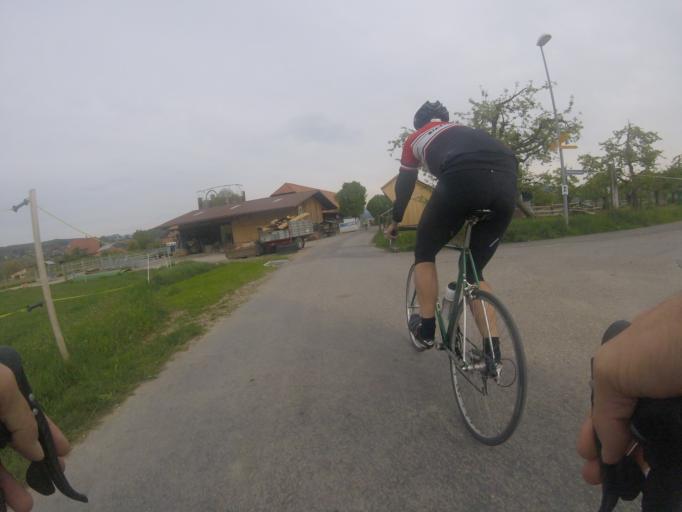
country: CH
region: Bern
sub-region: Bern-Mittelland District
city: Muri
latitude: 46.9154
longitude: 7.4890
